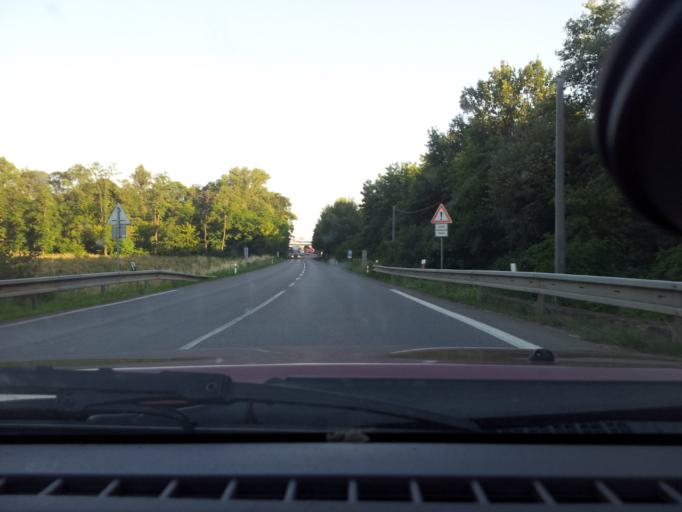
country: CZ
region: South Moravian
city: Hodonin
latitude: 48.8782
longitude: 17.1161
